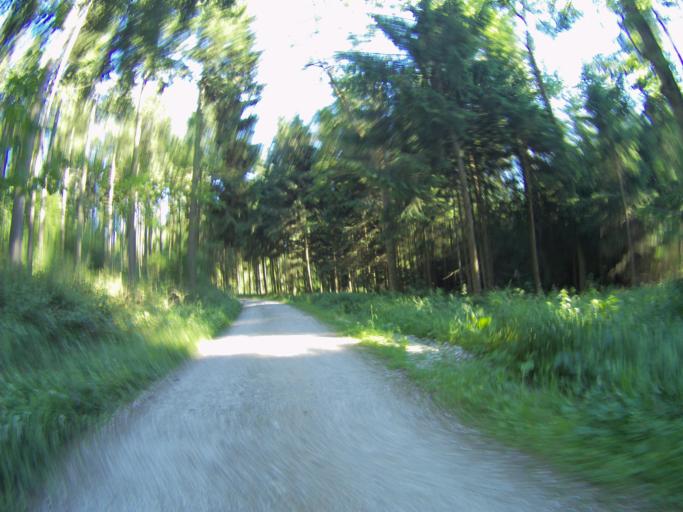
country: DE
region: Bavaria
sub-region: Upper Bavaria
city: Freising
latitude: 48.4178
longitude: 11.7000
